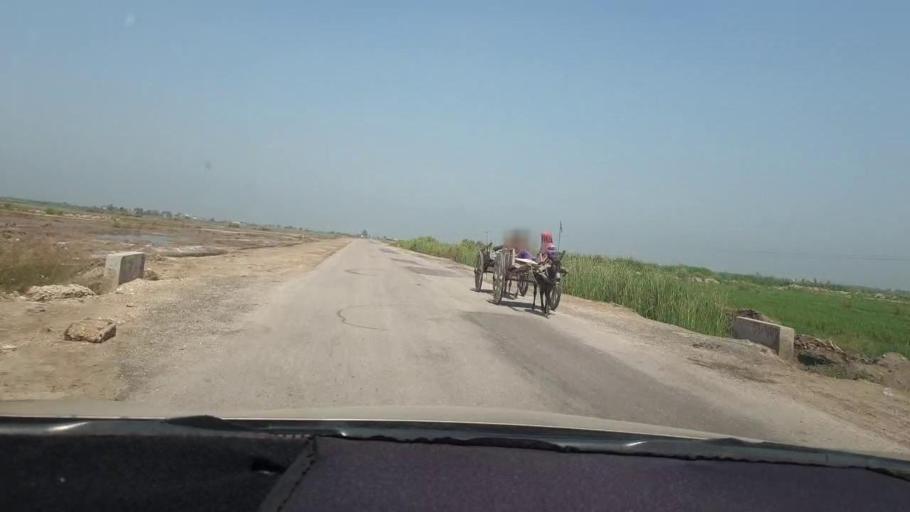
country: PK
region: Sindh
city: Miro Khan
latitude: 27.8307
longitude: 68.0151
